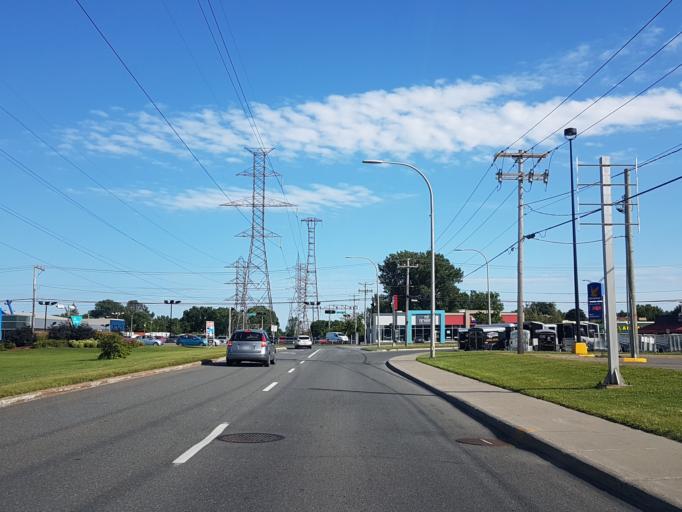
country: CA
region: Quebec
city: Sainte-Catherine
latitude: 46.3261
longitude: -72.5642
